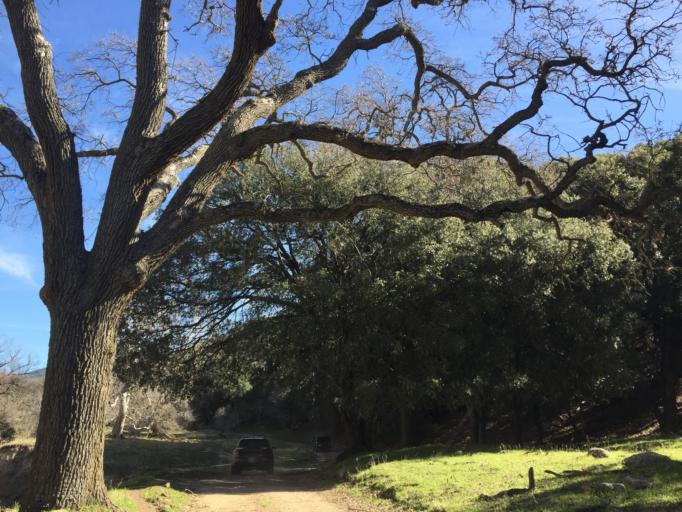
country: US
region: California
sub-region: Kern County
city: Lebec
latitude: 34.8887
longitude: -118.7550
